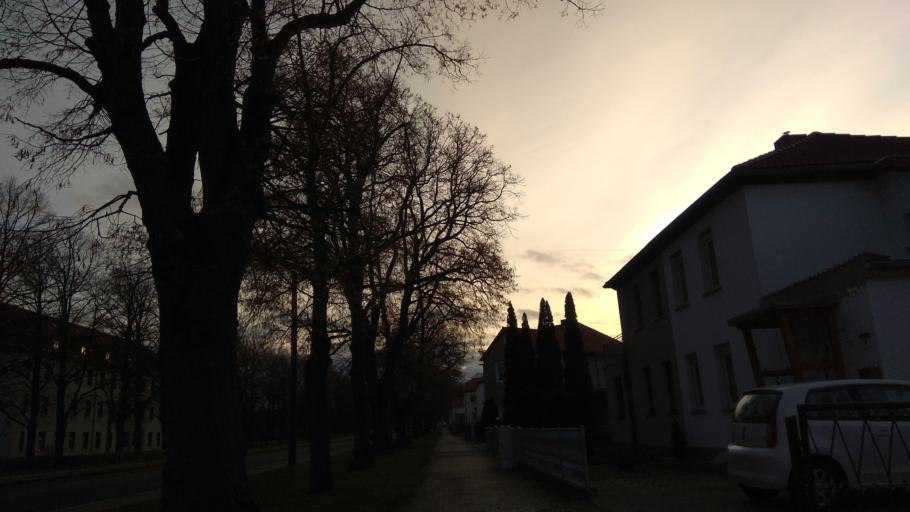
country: DE
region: Saxony-Anhalt
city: Halberstadt
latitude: 51.8768
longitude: 11.0534
